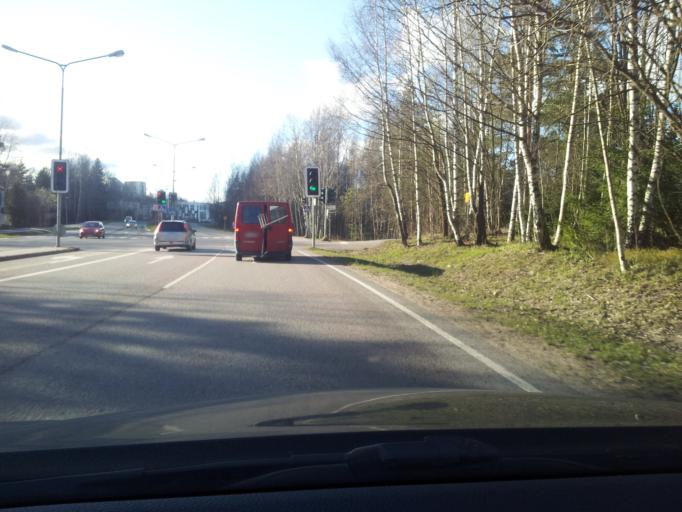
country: FI
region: Uusimaa
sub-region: Helsinki
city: Espoo
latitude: 60.1463
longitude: 24.6721
